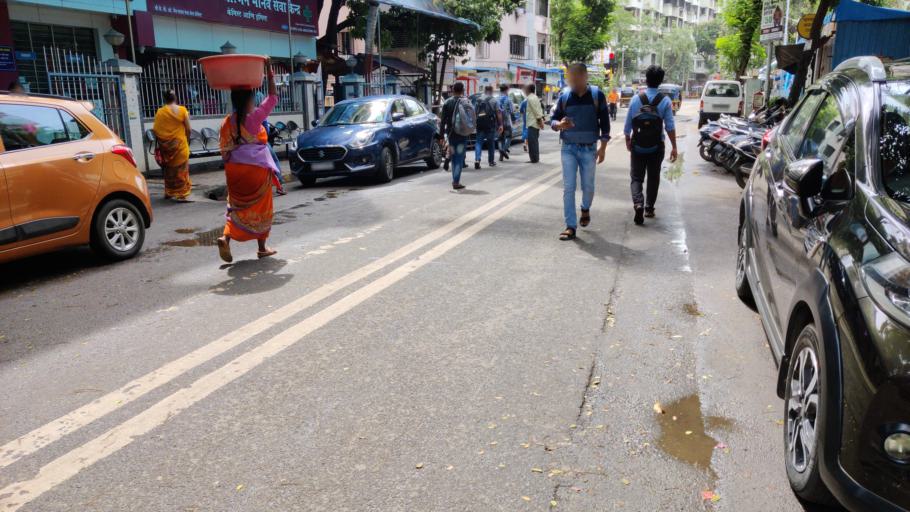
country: IN
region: Maharashtra
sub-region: Mumbai Suburban
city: Borivli
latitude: 19.2463
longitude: 72.8605
